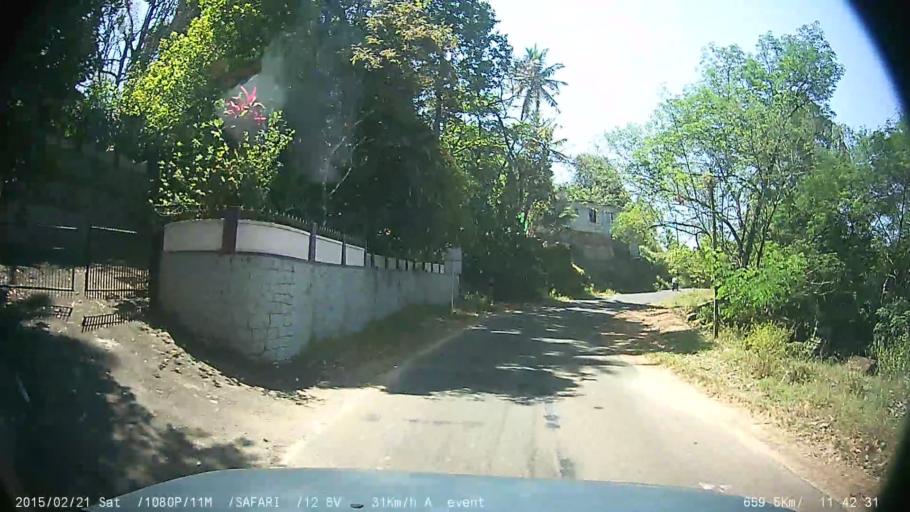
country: IN
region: Kerala
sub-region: Kottayam
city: Lalam
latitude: 9.7886
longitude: 76.7305
